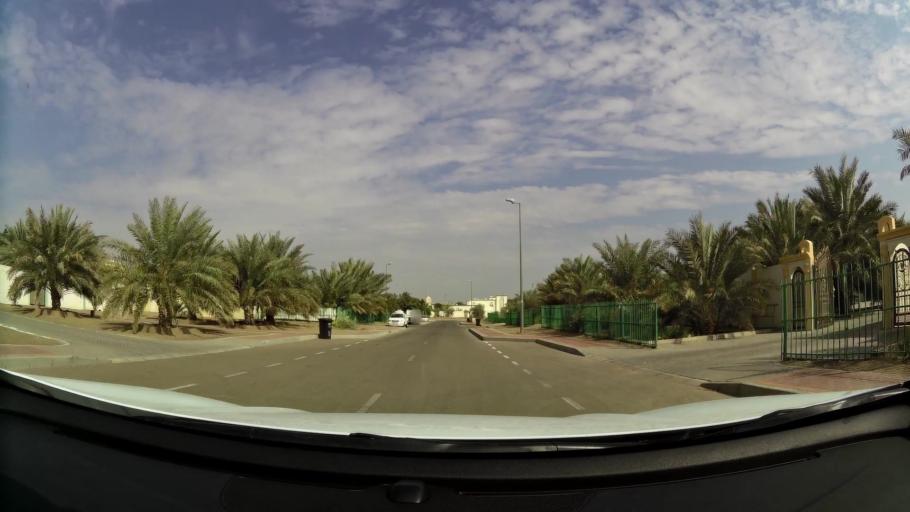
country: AE
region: Abu Dhabi
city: Al Ain
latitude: 24.0962
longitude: 55.9021
